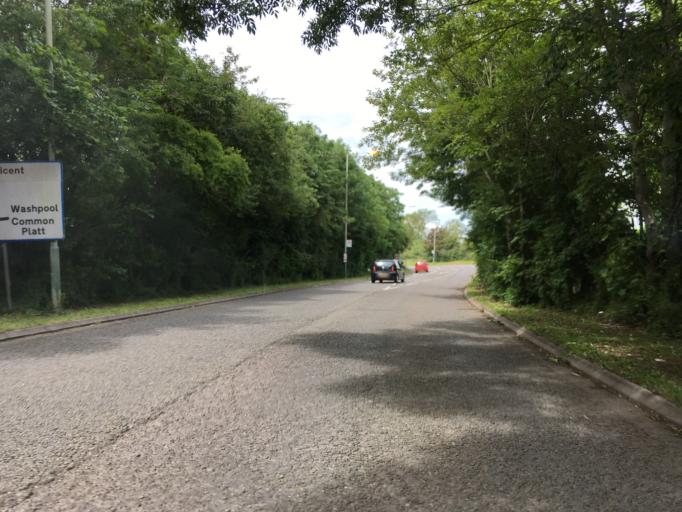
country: GB
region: England
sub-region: Wiltshire
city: Lydiard Tregoze
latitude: 51.5671
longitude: -1.8497
